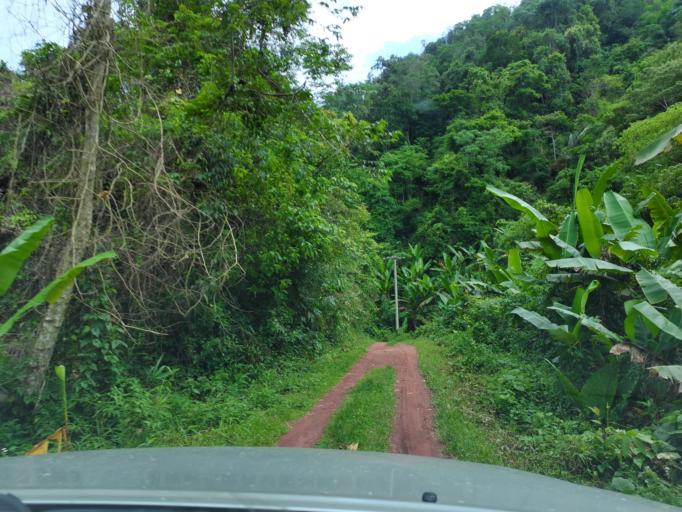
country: LA
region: Loungnamtha
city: Muang Nale
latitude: 20.5158
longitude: 101.0728
